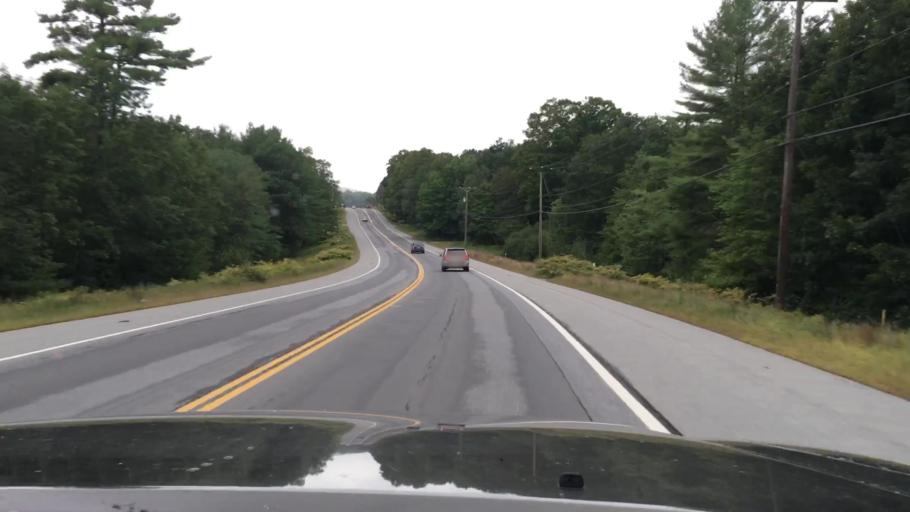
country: US
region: New Hampshire
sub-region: Cheshire County
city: Chesterfield
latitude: 42.8997
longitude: -72.4849
